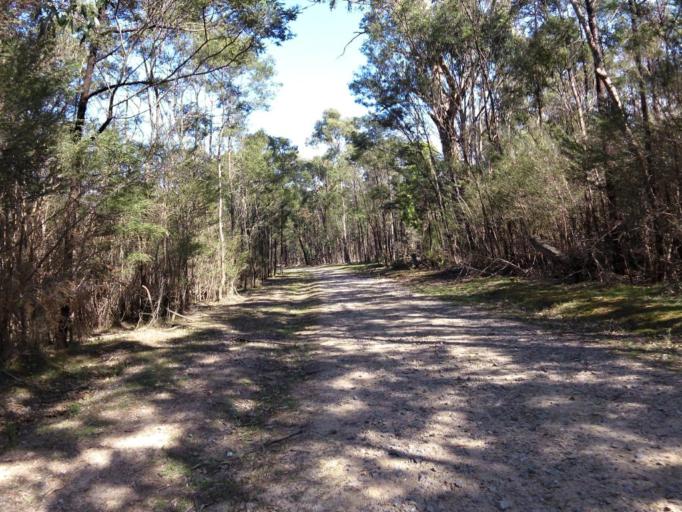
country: AU
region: Victoria
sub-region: Yarra Ranges
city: Lysterfield
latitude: -37.9405
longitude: 145.2890
